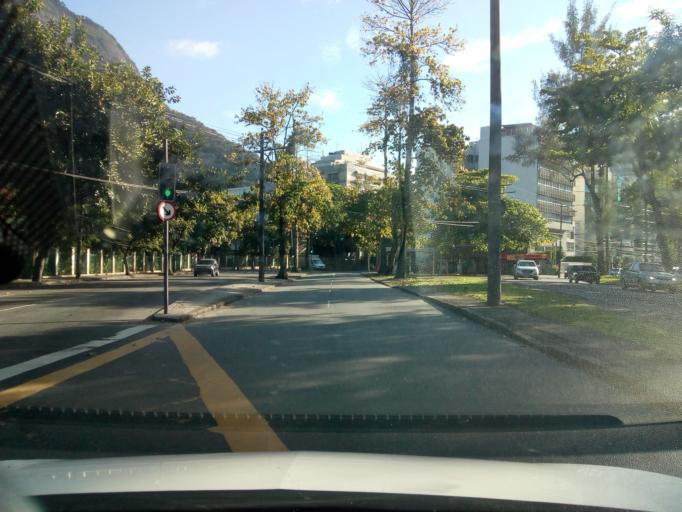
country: BR
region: Rio de Janeiro
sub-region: Rio De Janeiro
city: Rio de Janeiro
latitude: -22.9630
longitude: -43.2126
